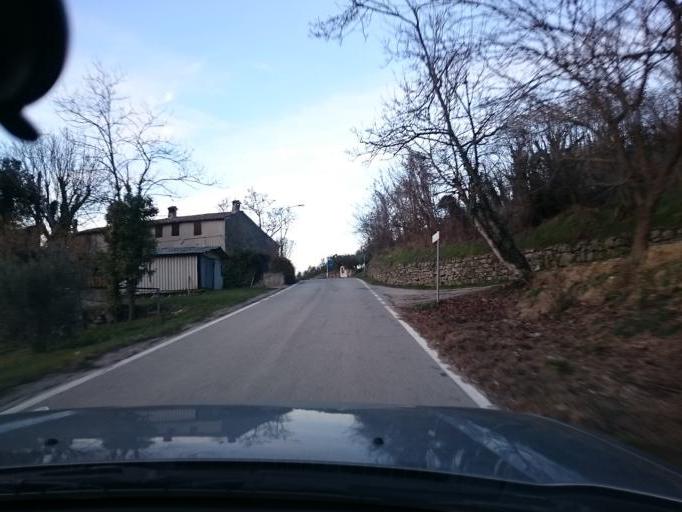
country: IT
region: Veneto
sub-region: Provincia di Padova
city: Fontanafredda
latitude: 45.3230
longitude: 11.6808
